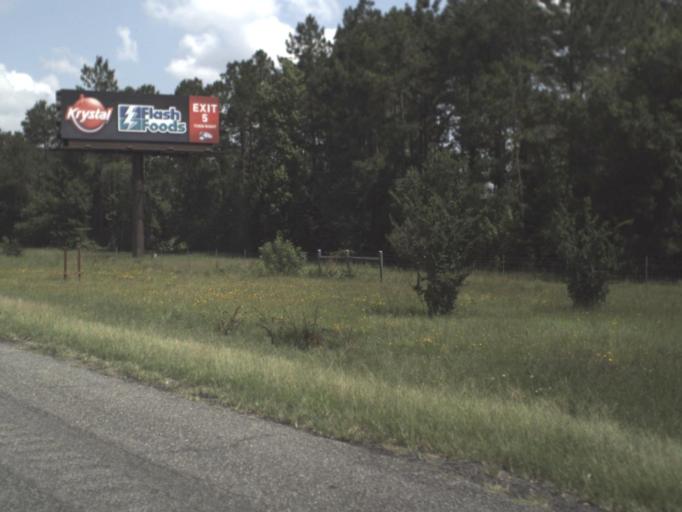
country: US
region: Georgia
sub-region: Echols County
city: Statenville
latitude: 30.6272
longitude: -83.1734
